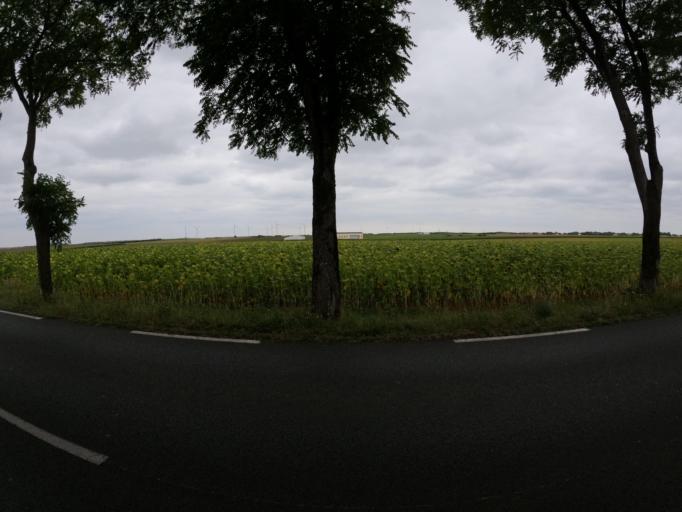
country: FR
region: Pays de la Loire
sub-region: Departement de la Vendee
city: Serigne
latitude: 46.4830
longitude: -0.8867
